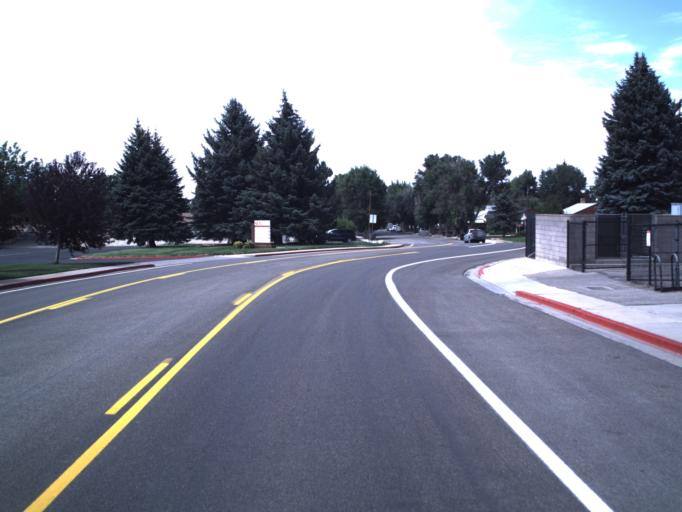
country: US
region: Utah
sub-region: Iron County
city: Cedar City
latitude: 37.6760
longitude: -113.0779
